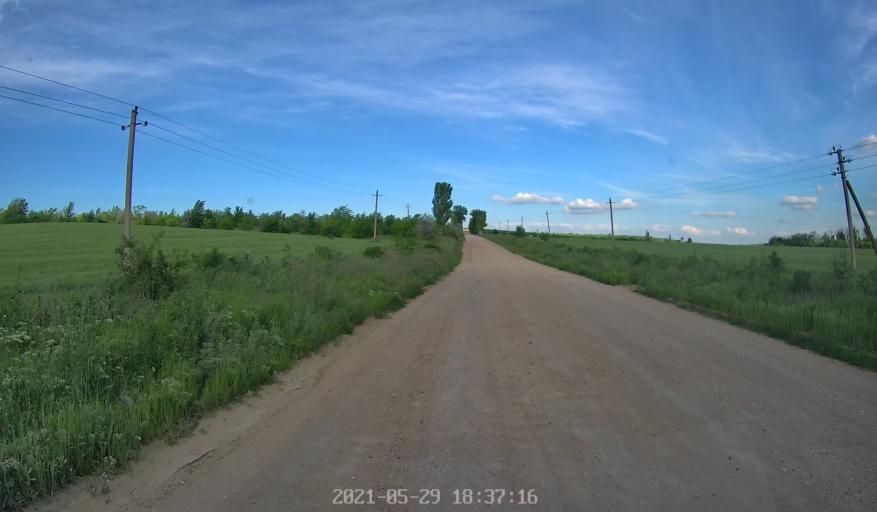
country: MD
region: Chisinau
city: Singera
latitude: 46.8046
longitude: 28.9297
